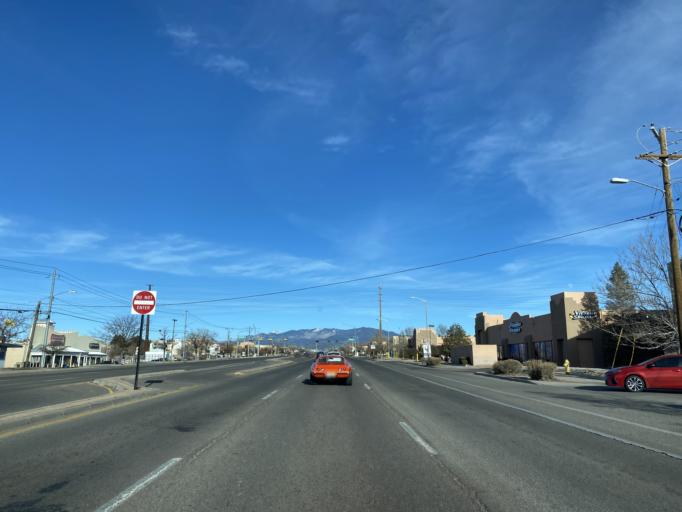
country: US
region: New Mexico
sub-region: Santa Fe County
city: Agua Fria
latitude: 35.6412
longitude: -106.0143
